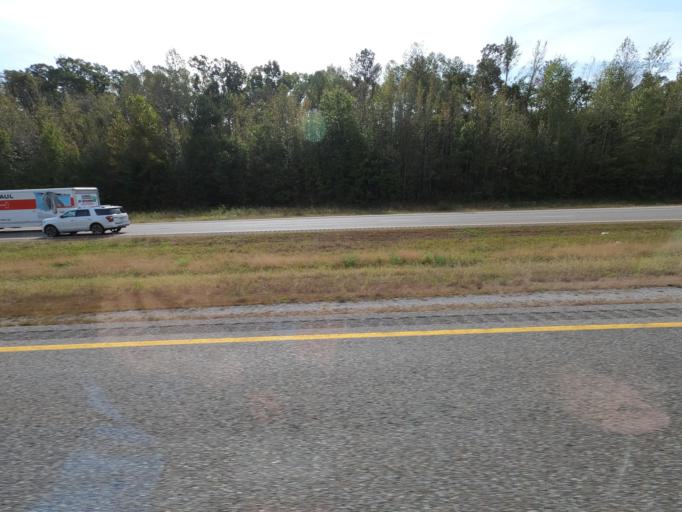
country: US
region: Tennessee
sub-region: Humphreys County
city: New Johnsonville
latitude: 35.8659
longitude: -87.9309
